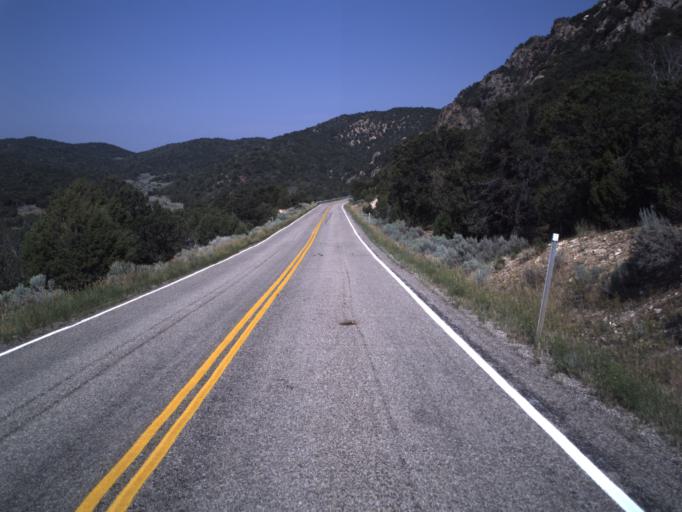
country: US
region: Utah
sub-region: Daggett County
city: Manila
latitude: 40.9526
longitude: -109.4635
